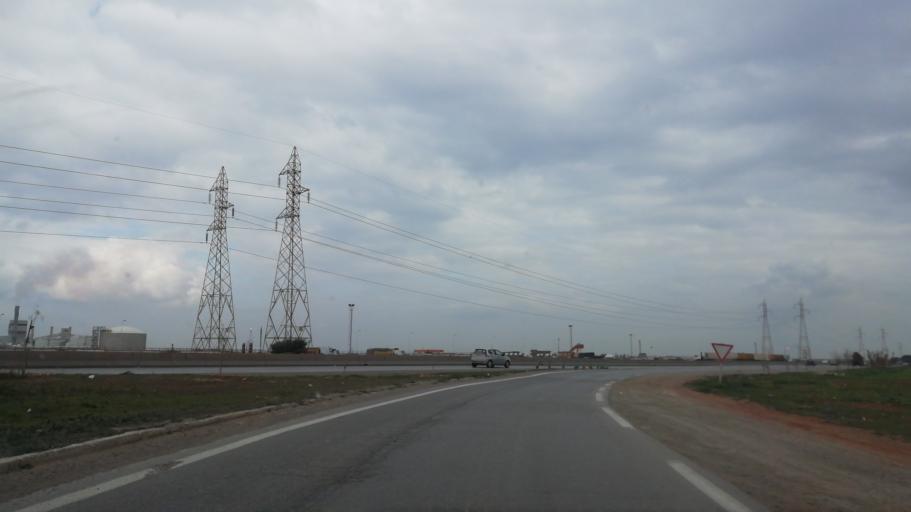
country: DZ
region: Oran
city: Ain el Bya
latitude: 35.7993
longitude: -0.3438
